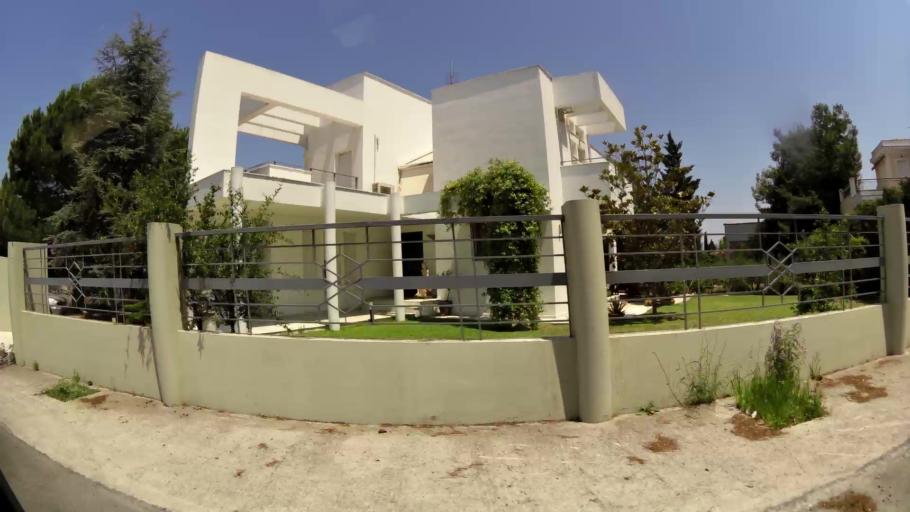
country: GR
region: Central Macedonia
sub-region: Nomos Thessalonikis
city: Plagiari
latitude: 40.4778
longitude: 22.9576
